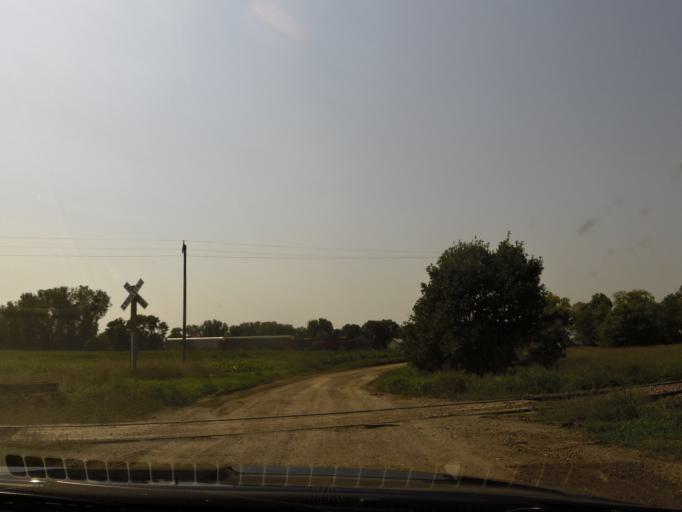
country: US
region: North Dakota
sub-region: Ransom County
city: Sheldon
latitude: 46.2680
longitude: -97.1274
